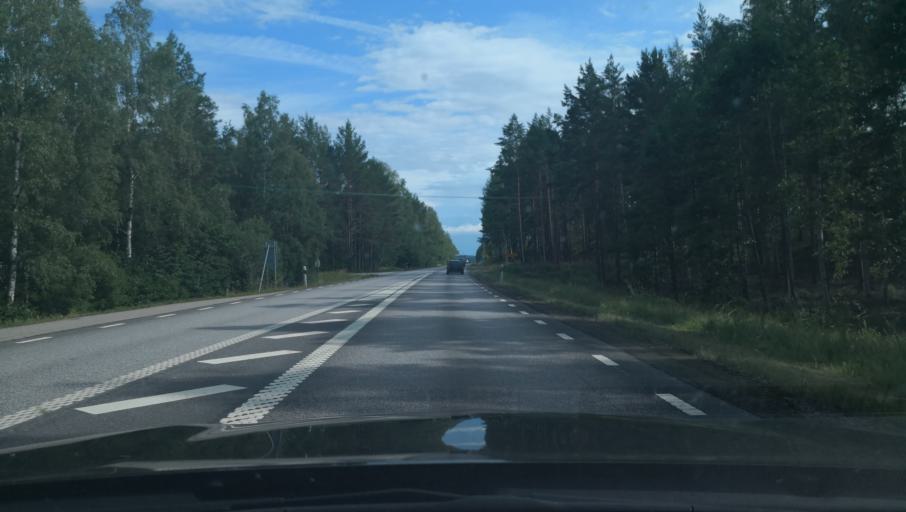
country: SE
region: Kalmar
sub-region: Vimmerby Kommun
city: Sodra Vi
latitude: 57.8682
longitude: 15.7397
